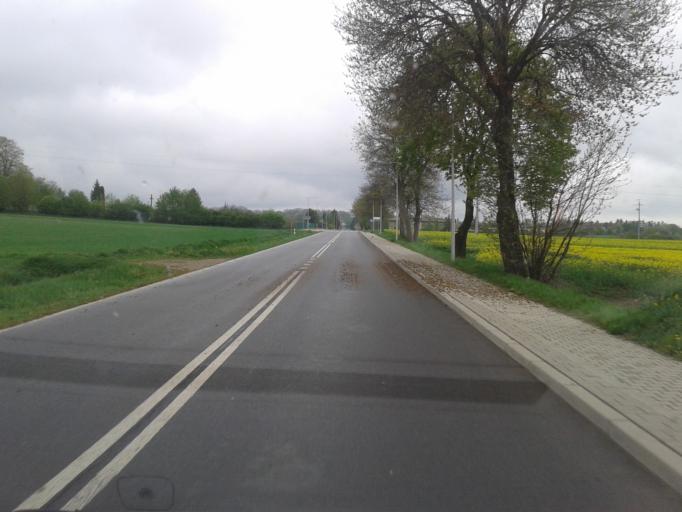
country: PL
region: Lublin Voivodeship
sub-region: Powiat hrubieszowski
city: Dolhobyczow
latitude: 50.5850
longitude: 24.0481
